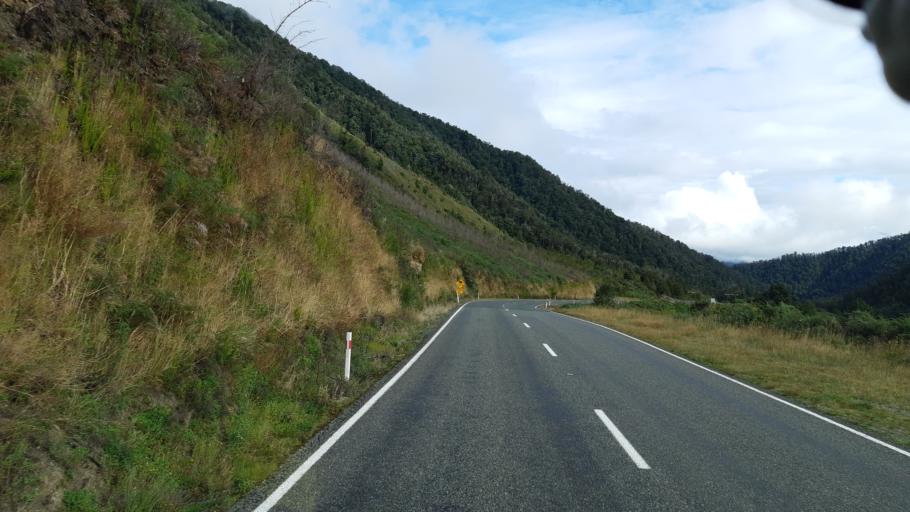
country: NZ
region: West Coast
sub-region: Buller District
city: Westport
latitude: -42.0046
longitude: 172.2313
